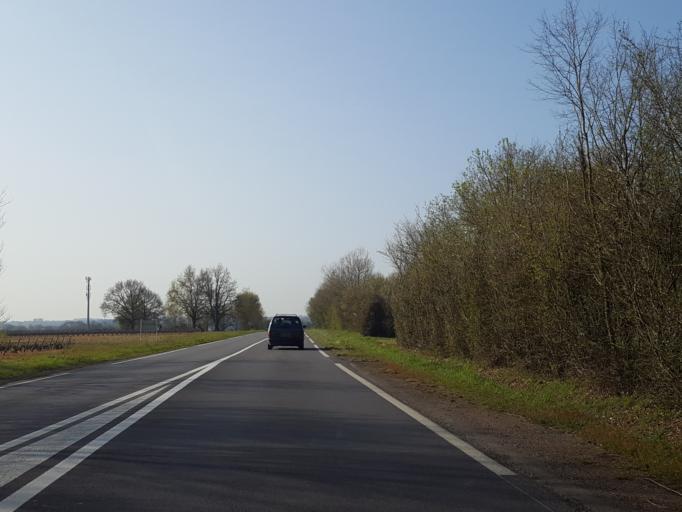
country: FR
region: Pays de la Loire
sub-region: Departement de la Vendee
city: Saint-Philbert-de-Bouaine
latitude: 46.9915
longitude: -1.5164
